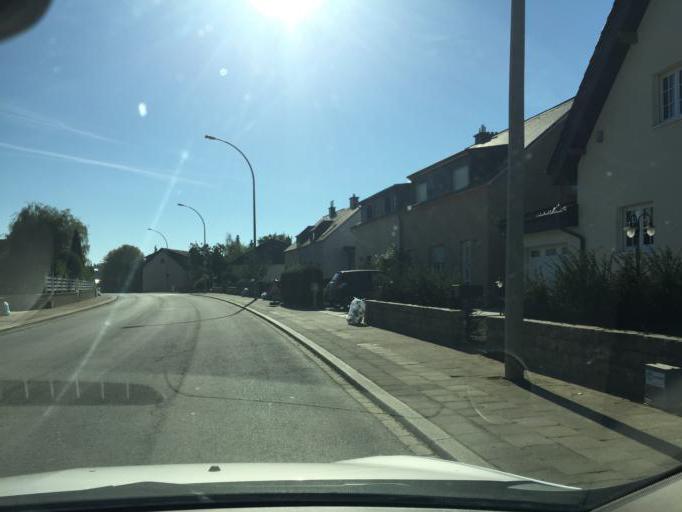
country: LU
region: Luxembourg
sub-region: Canton de Luxembourg
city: Contern
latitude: 49.5876
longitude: 6.2211
